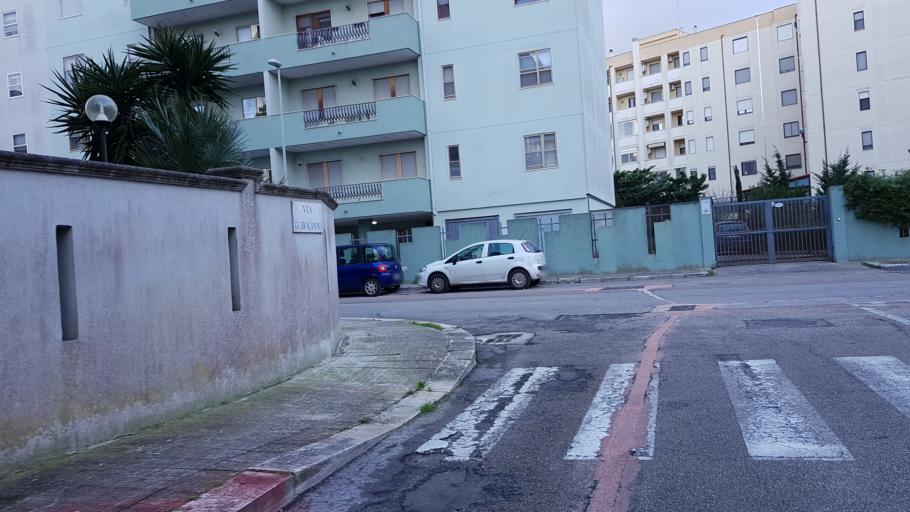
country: IT
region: Apulia
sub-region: Provincia di Brindisi
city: Brindisi
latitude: 40.6177
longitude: 17.9191
